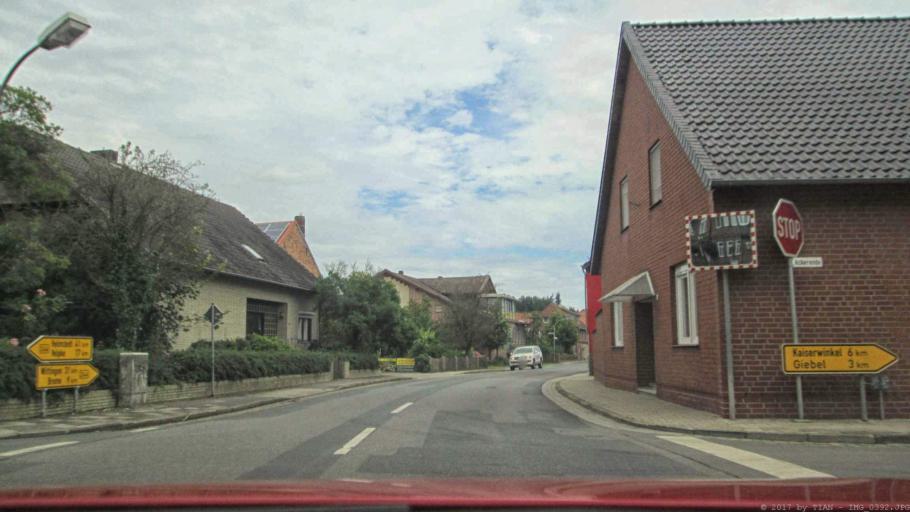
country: DE
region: Lower Saxony
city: Parsau
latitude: 52.5334
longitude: 10.8912
